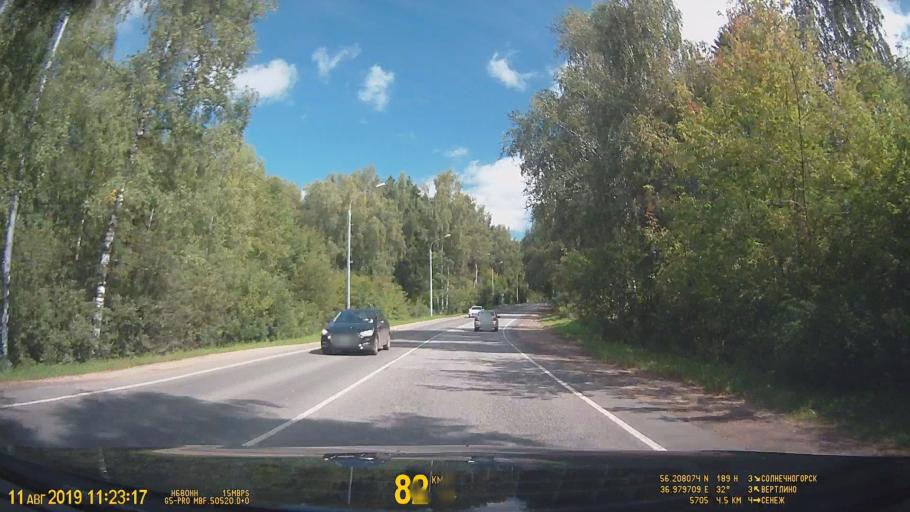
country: RU
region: Moskovskaya
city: Solnechnogorsk
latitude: 56.2083
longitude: 36.9800
